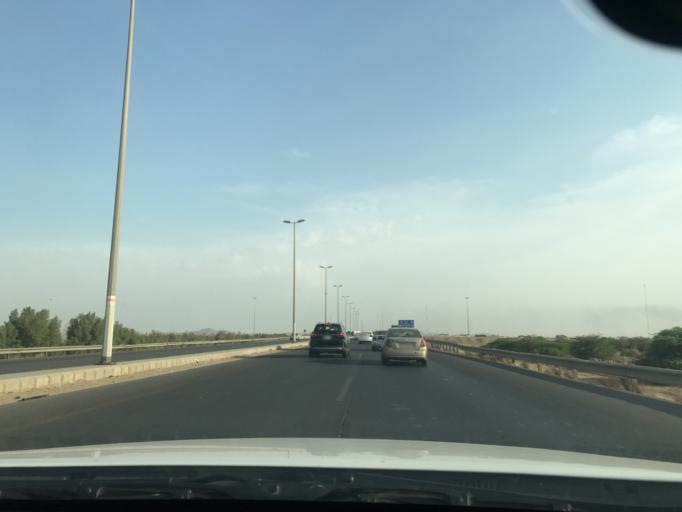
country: SA
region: Makkah
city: Jeddah
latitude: 21.3930
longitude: 39.4268
